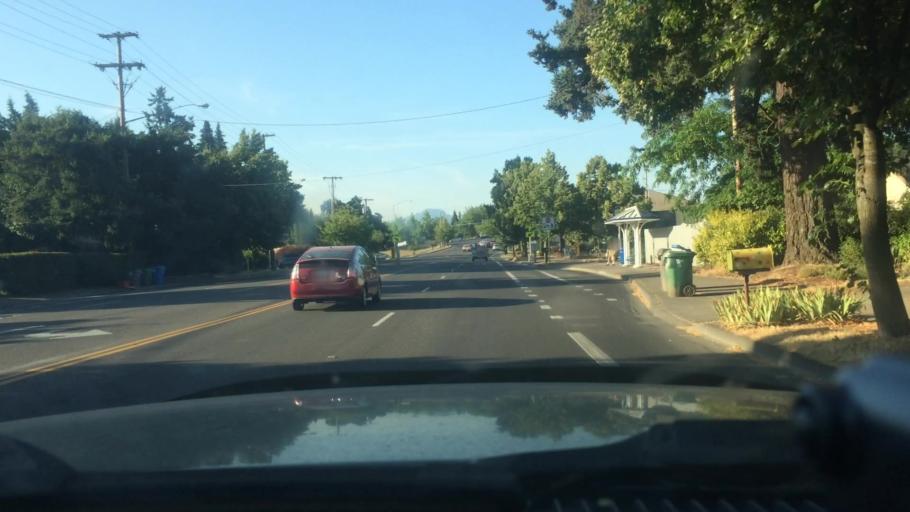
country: US
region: Oregon
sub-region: Lane County
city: Eugene
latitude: 44.0667
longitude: -123.1178
